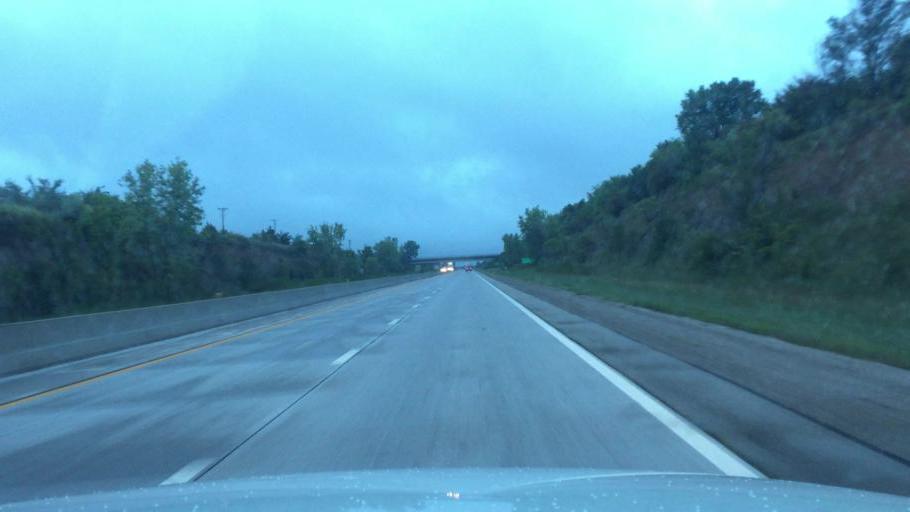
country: US
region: Kansas
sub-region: Neosho County
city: Chanute
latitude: 37.6793
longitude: -95.4796
